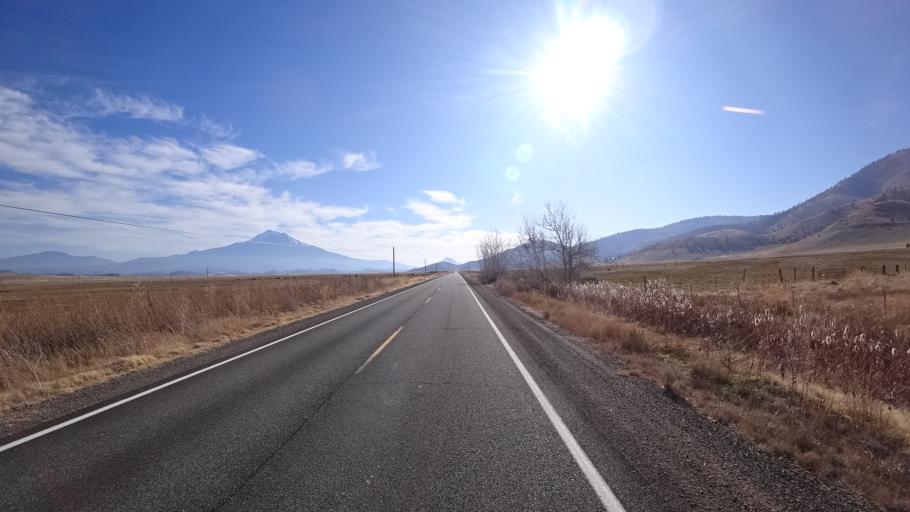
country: US
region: California
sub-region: Siskiyou County
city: Weed
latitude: 41.4910
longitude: -122.5071
